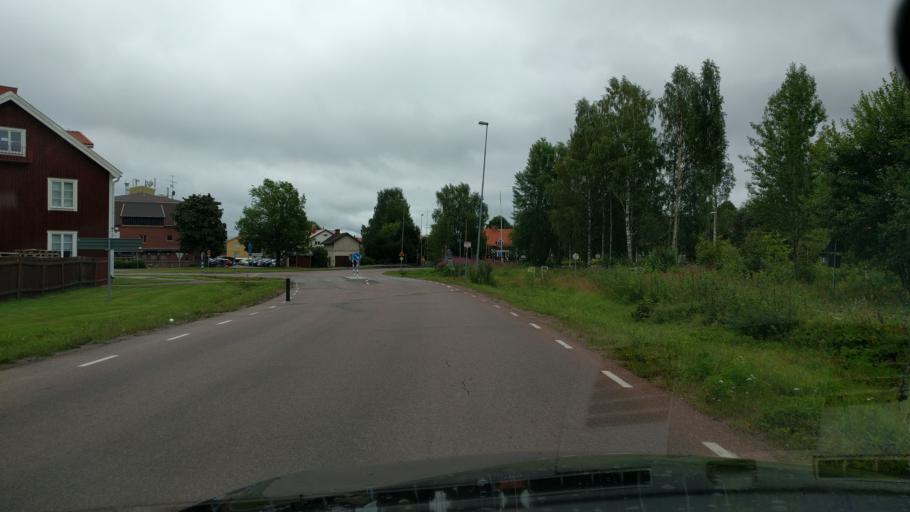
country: SE
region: Dalarna
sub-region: Mora Kommun
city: Mora
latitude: 61.0023
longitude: 14.5321
